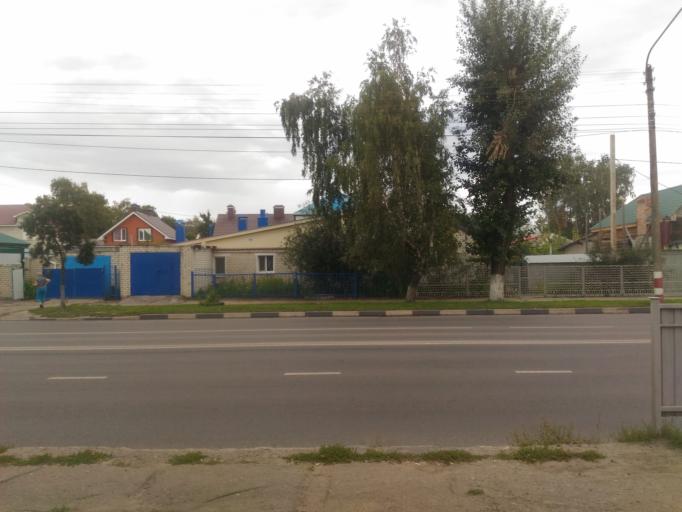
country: RU
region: Ulyanovsk
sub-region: Ulyanovskiy Rayon
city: Ulyanovsk
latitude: 54.2744
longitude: 48.3330
